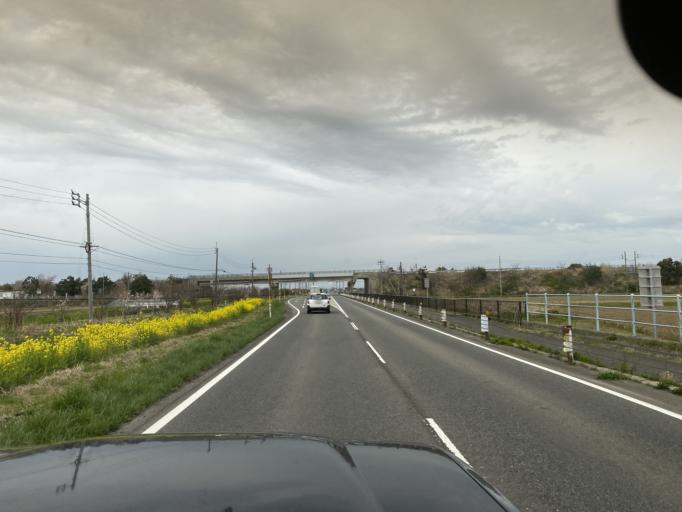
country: JP
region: Niigata
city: Niitsu-honcho
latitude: 37.8189
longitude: 139.0994
